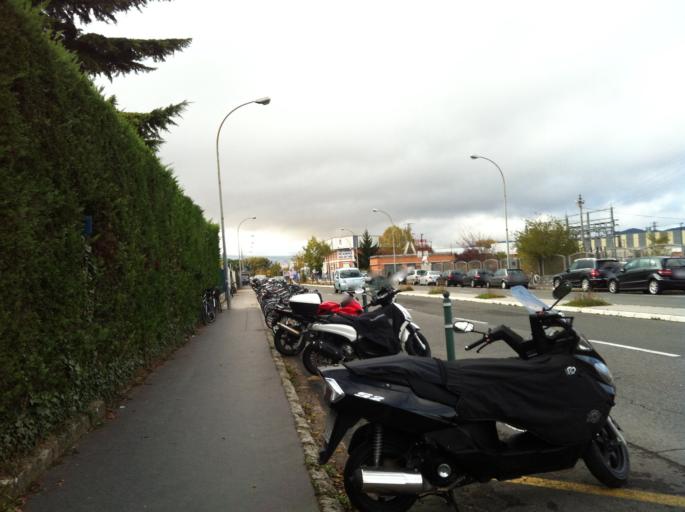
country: ES
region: Basque Country
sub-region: Provincia de Alava
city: Gasteiz / Vitoria
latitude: 42.8565
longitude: -2.7128
